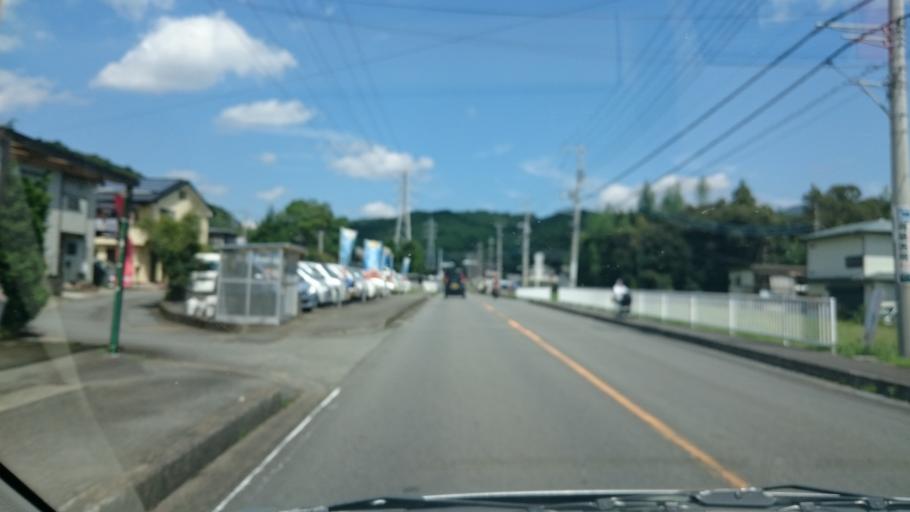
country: JP
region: Shizuoka
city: Mishima
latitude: 35.1962
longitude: 138.9237
